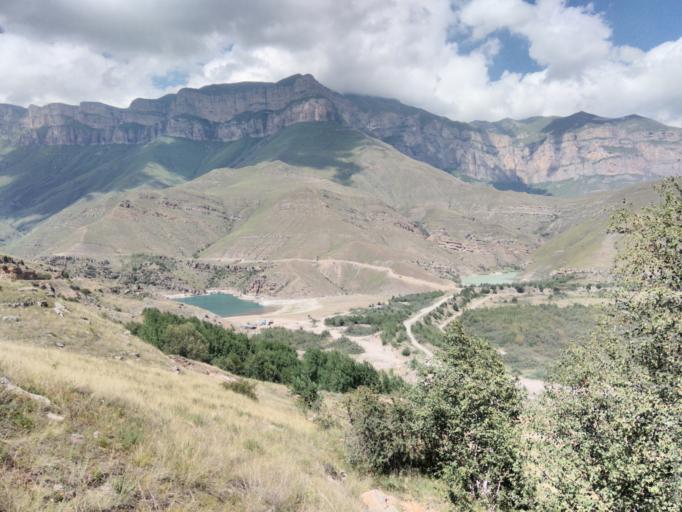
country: RU
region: Kabardino-Balkariya
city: Bylym
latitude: 43.4570
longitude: 42.9932
